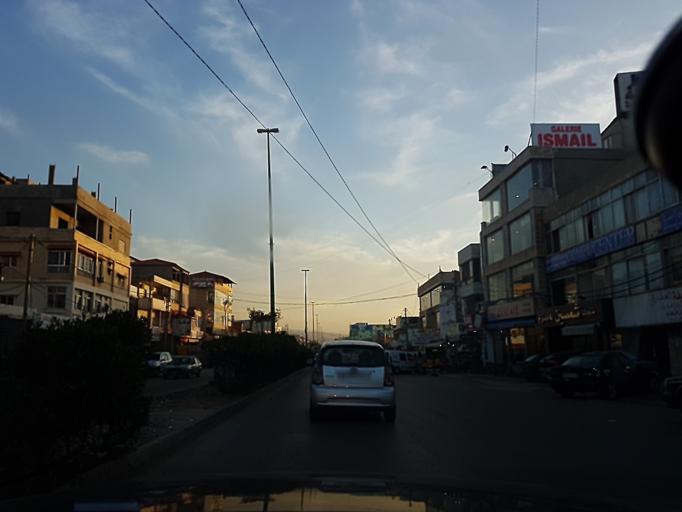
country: LB
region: Beyrouth
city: Beirut
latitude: 33.8435
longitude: 35.4849
